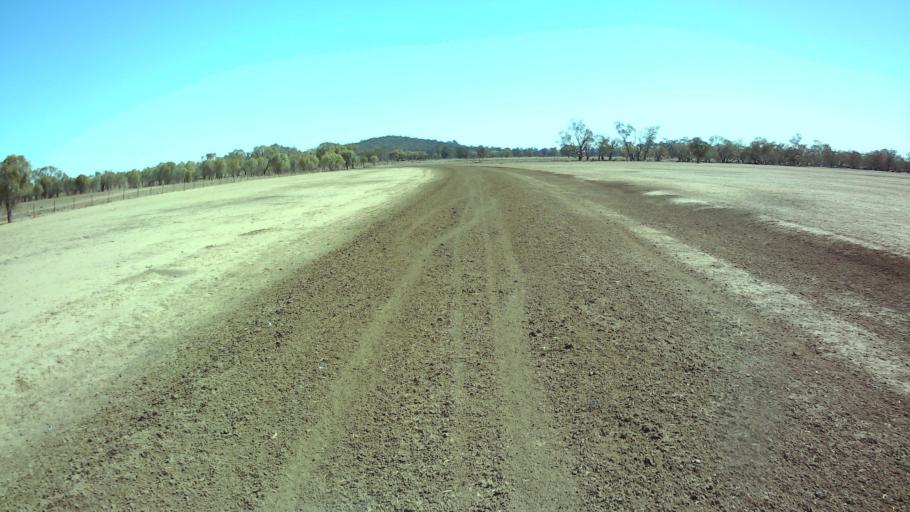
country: AU
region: New South Wales
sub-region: Bland
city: West Wyalong
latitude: -33.7529
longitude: 147.6595
